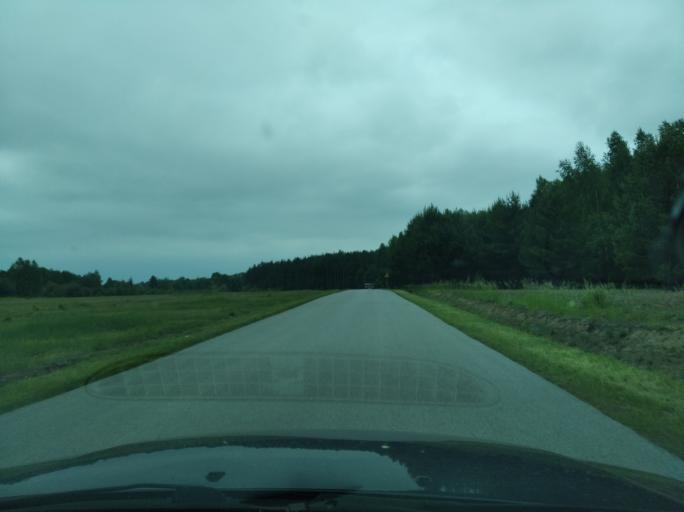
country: PL
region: Subcarpathian Voivodeship
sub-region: Powiat kolbuszowski
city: Niwiska
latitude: 50.2133
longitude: 21.6358
